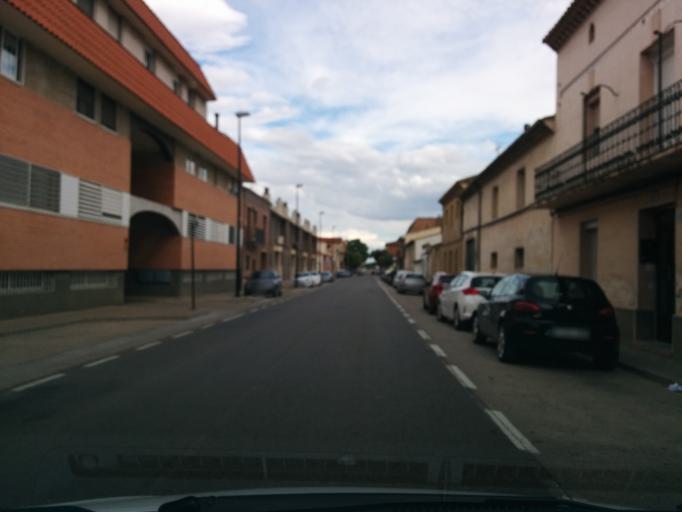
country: ES
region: Aragon
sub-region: Provincia de Zaragoza
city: Zaragoza
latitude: 41.6508
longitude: -0.8264
